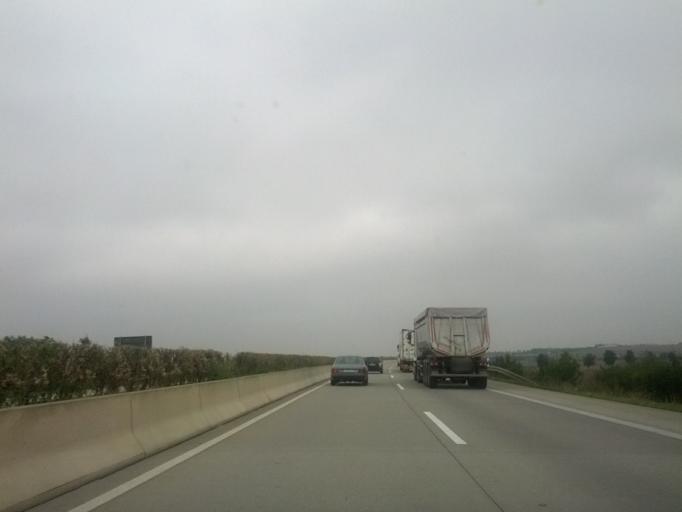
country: DE
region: Thuringia
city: Zimmernsupra
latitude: 50.9866
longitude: 10.9110
